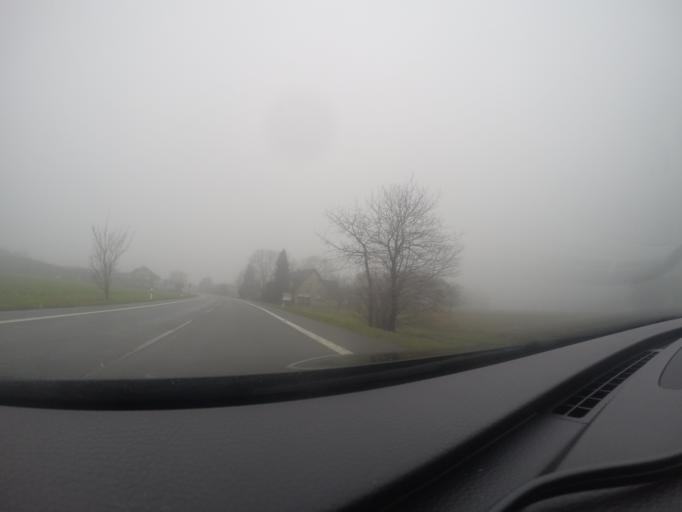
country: DE
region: North Rhine-Westphalia
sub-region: Regierungsbezirk Dusseldorf
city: Bocholt
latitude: 51.8623
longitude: 6.5694
